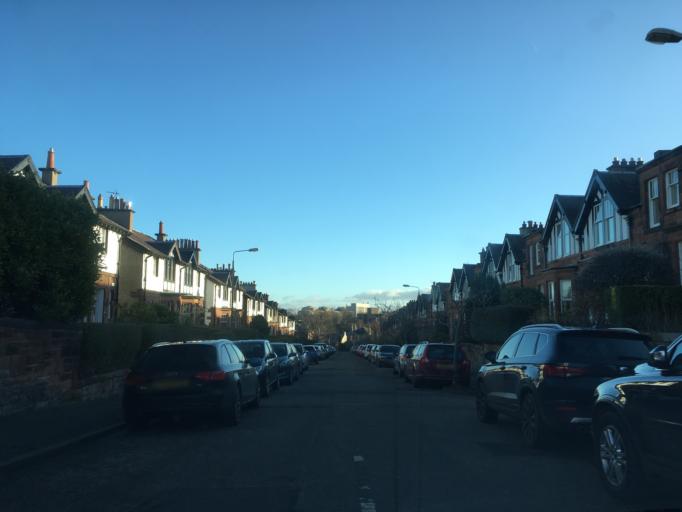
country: GB
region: Scotland
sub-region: Edinburgh
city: Colinton
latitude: 55.9595
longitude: -3.2518
